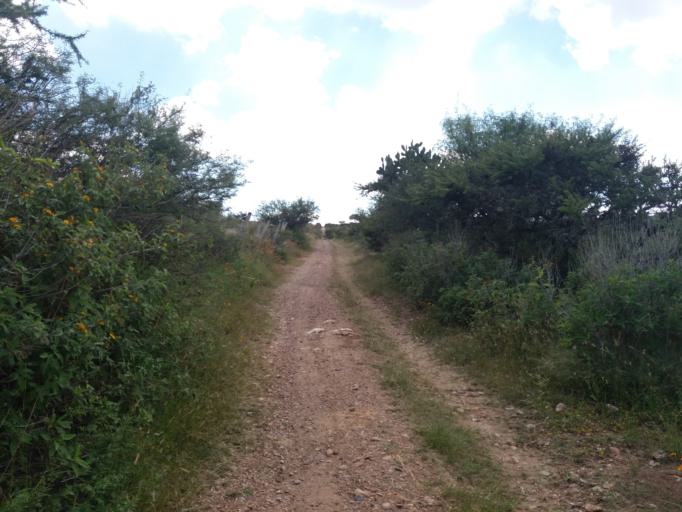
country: MX
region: Aguascalientes
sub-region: Aguascalientes
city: San Sebastian [Fraccionamiento]
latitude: 21.8039
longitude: -102.2425
